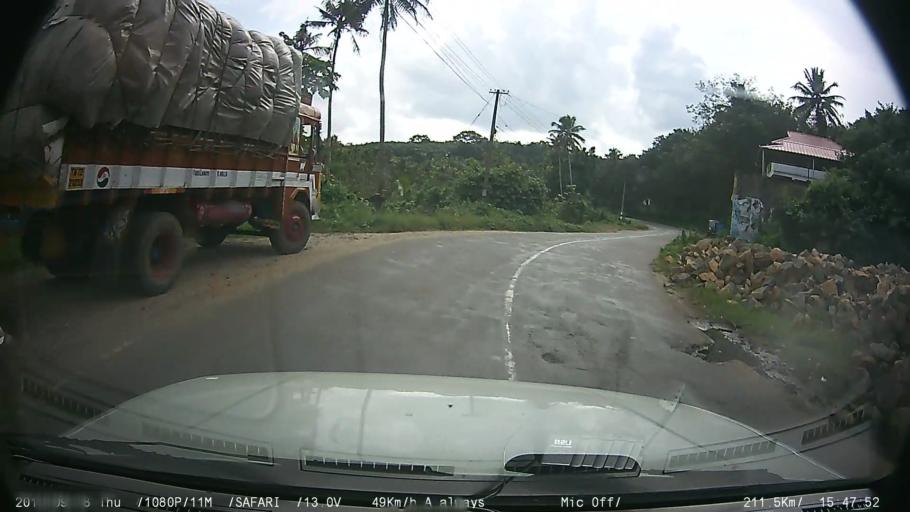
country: IN
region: Kerala
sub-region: Kottayam
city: Palackattumala
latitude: 9.8298
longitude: 76.5932
